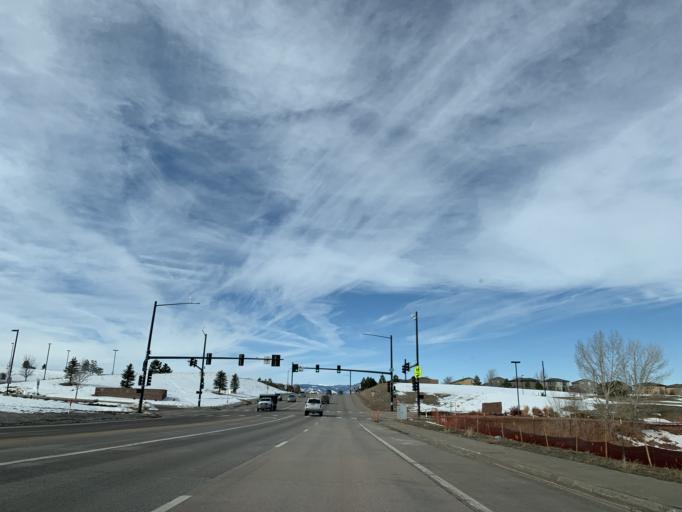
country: US
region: Colorado
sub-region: Douglas County
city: Carriage Club
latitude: 39.5218
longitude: -104.9204
